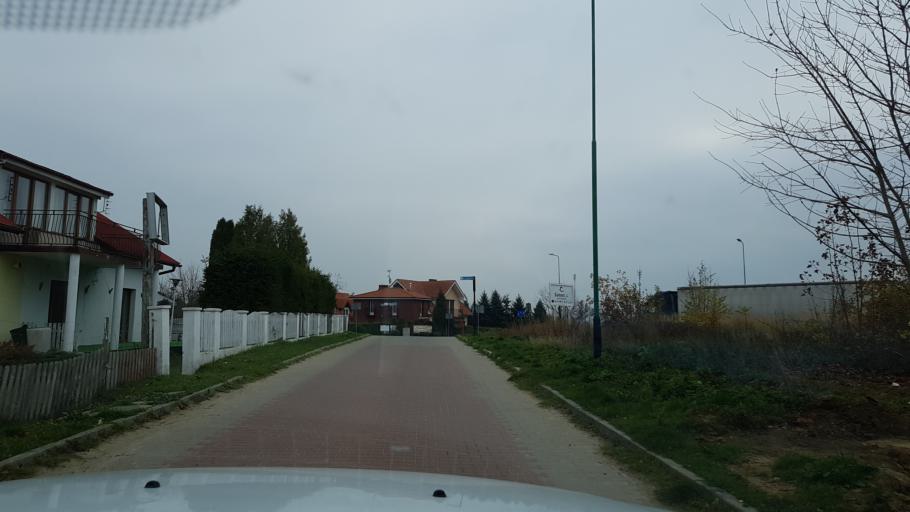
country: PL
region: West Pomeranian Voivodeship
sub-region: Powiat gryficki
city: Rewal
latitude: 54.0839
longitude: 15.0270
